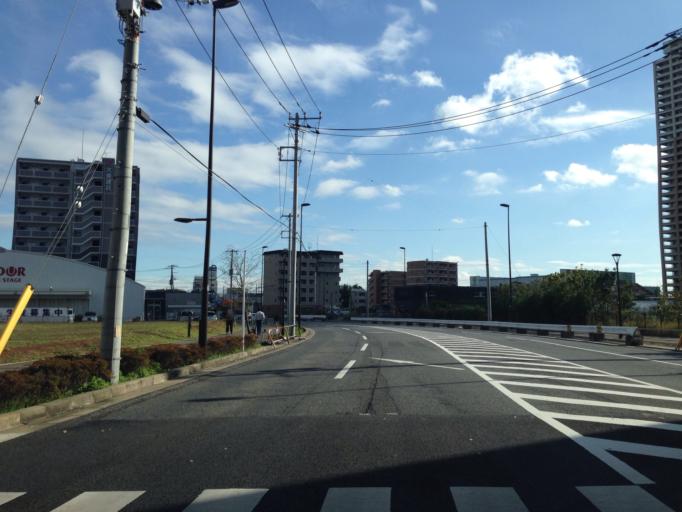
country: JP
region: Chiba
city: Kashiwa
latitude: 35.8959
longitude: 139.9531
